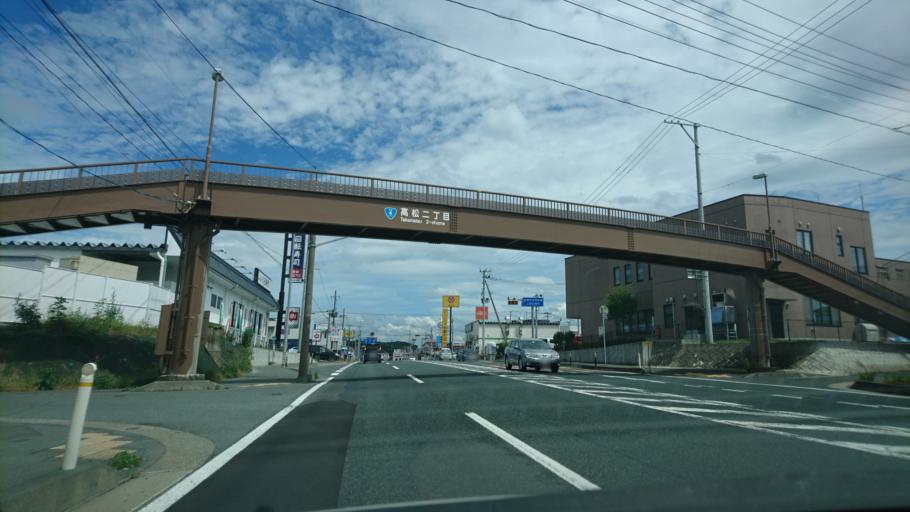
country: JP
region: Iwate
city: Morioka-shi
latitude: 39.7238
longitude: 141.1312
